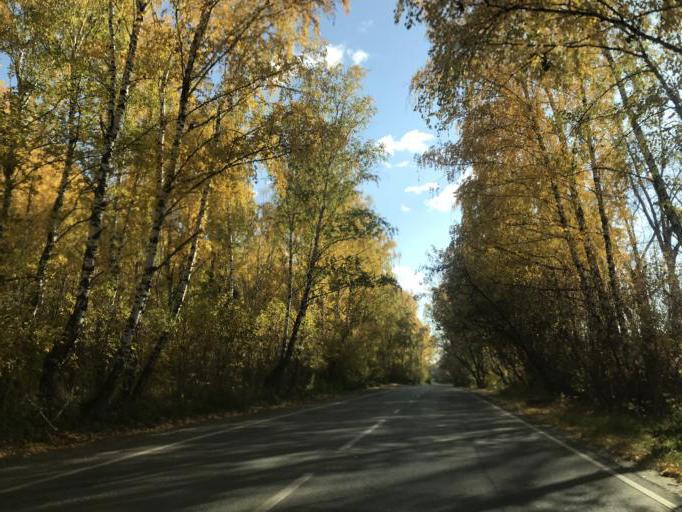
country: RU
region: Chelyabinsk
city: Dolgoderevenskoye
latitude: 55.2614
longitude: 61.3640
